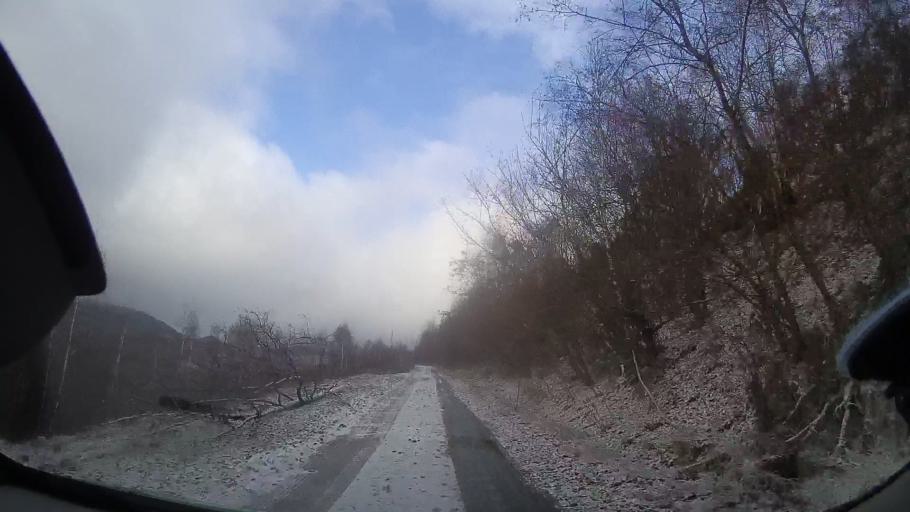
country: RO
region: Cluj
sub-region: Comuna Valea Ierii
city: Valea Ierii
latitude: 46.6514
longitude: 23.3546
